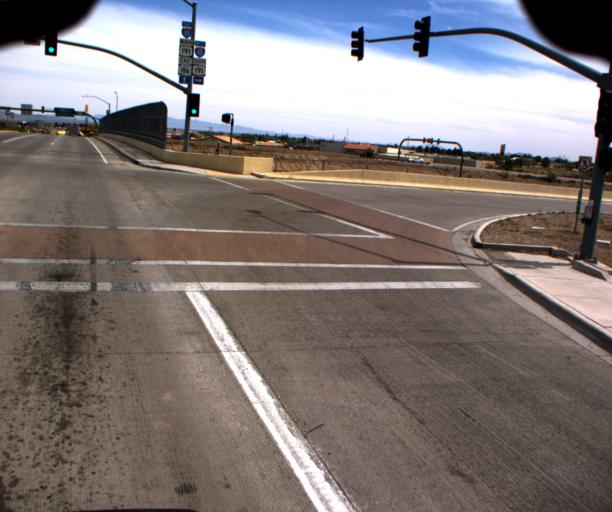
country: US
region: Arizona
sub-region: Cochise County
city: Willcox
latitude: 32.2668
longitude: -109.8447
